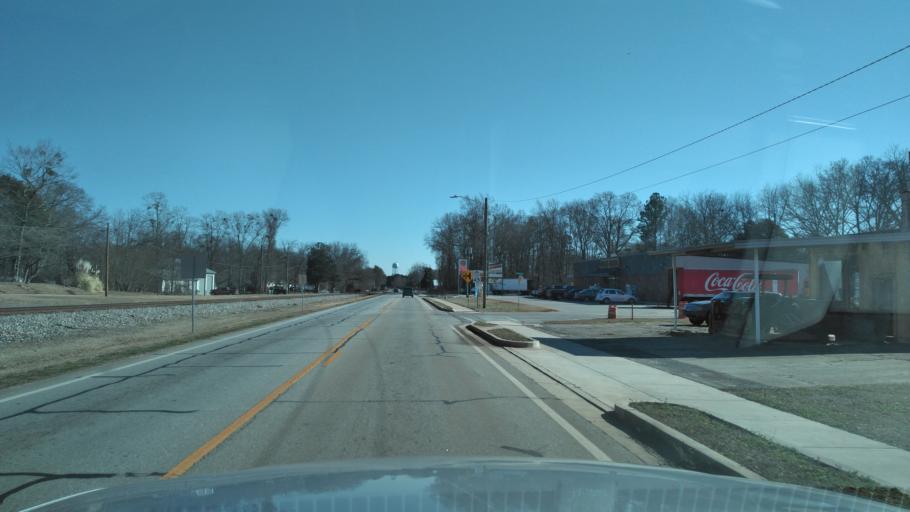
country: US
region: Georgia
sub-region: Banks County
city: Maysville
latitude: 34.2516
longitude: -83.5607
